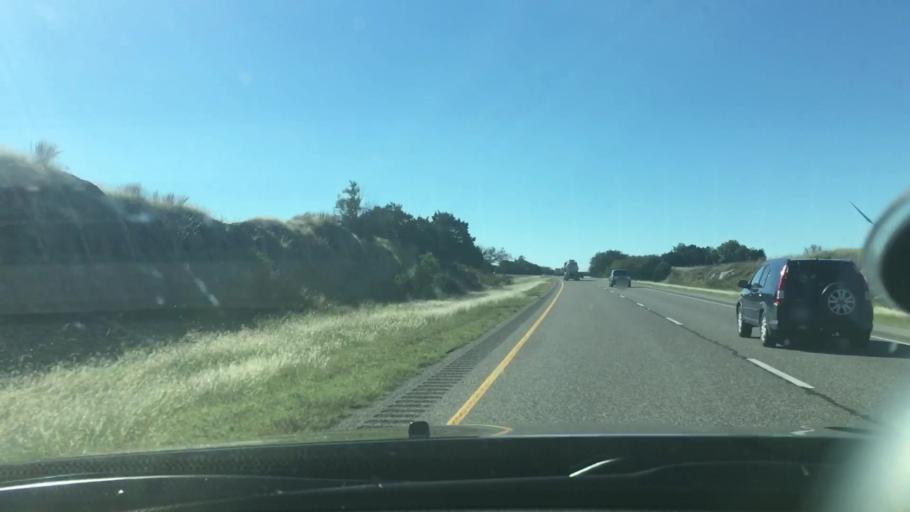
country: US
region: Oklahoma
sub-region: Murray County
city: Davis
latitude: 34.3931
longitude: -97.1421
